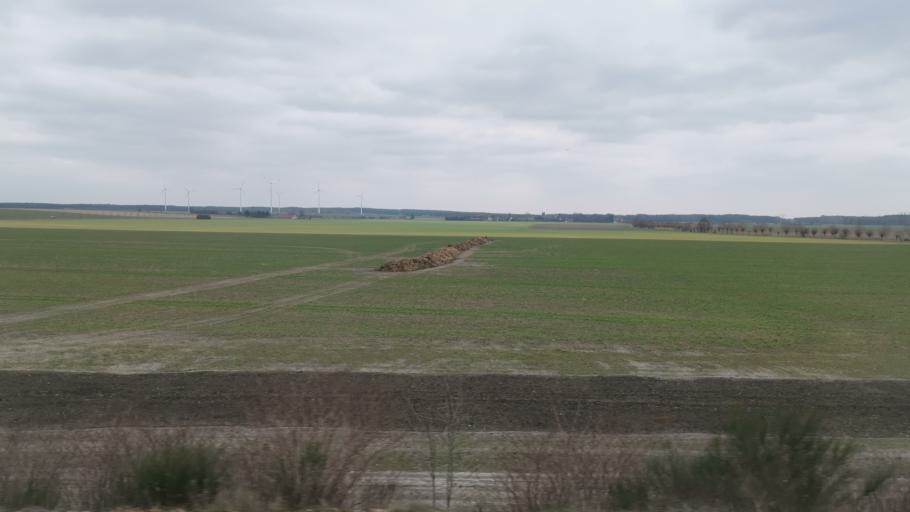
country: DE
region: Brandenburg
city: Doberlug-Kirchhain
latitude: 51.6152
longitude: 13.5627
